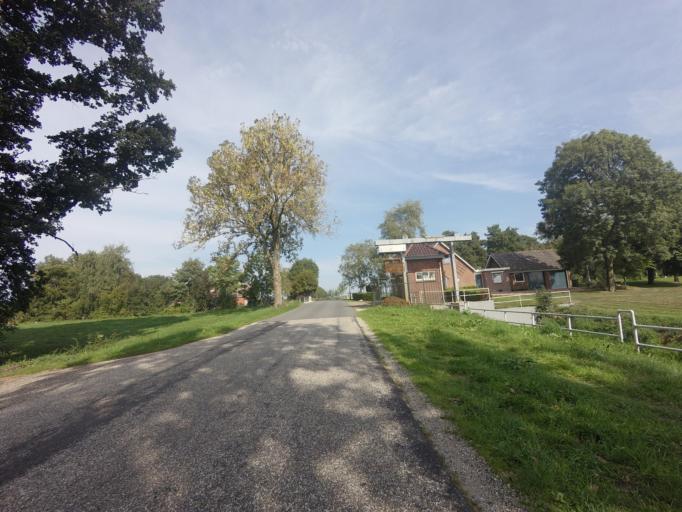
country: NL
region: Groningen
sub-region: Gemeente Leek
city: Leek
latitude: 53.2014
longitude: 6.3502
